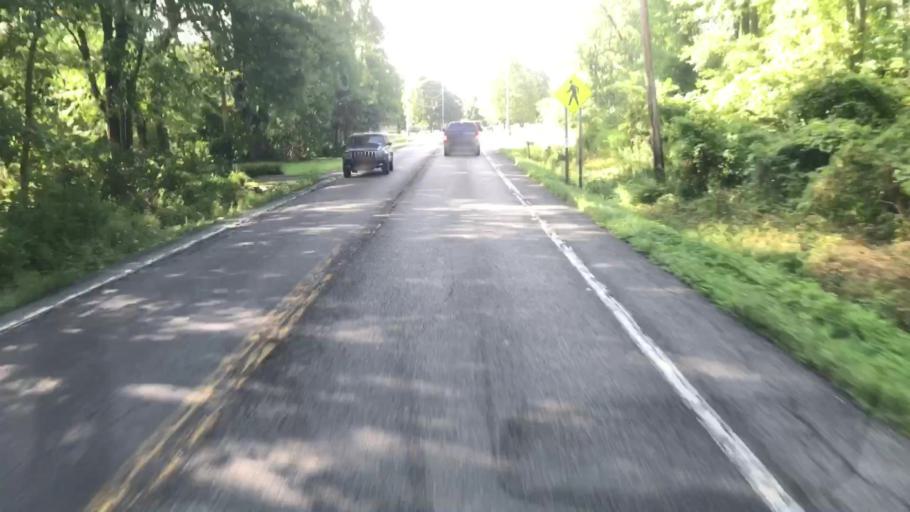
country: US
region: New York
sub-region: Onondaga County
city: Skaneateles
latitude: 42.9554
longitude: -76.4258
